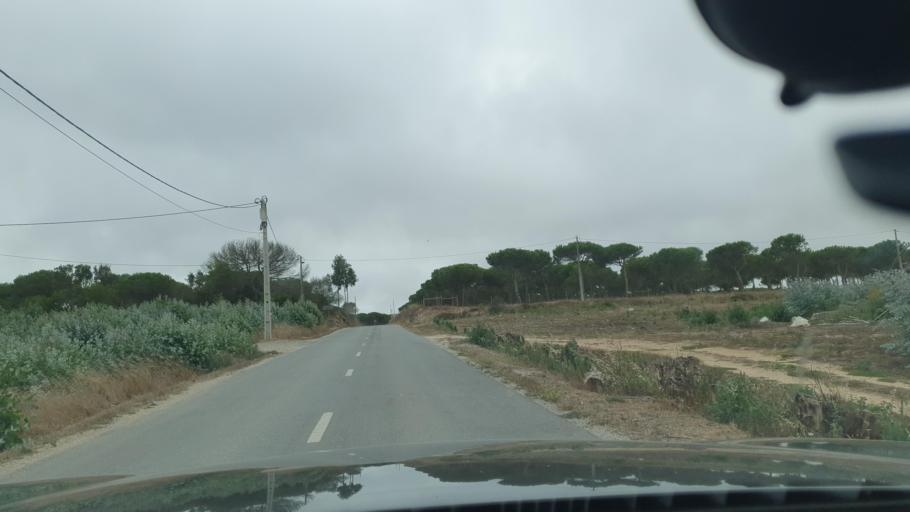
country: PT
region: Beja
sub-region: Odemira
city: Sao Teotonio
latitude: 37.5951
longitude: -8.7603
